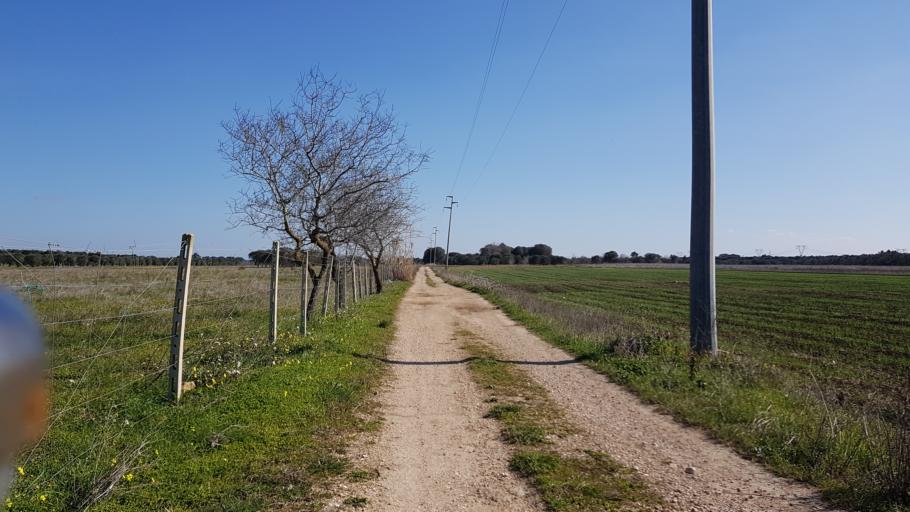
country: IT
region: Apulia
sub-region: Provincia di Brindisi
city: Mesagne
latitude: 40.6119
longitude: 17.7992
